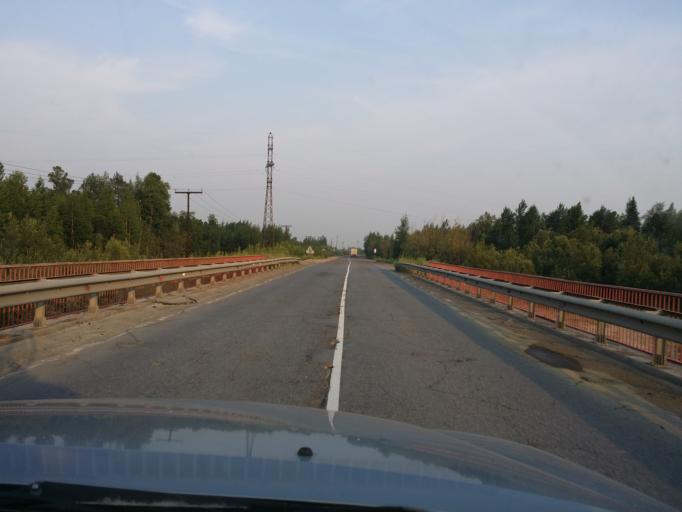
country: RU
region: Khanty-Mansiyskiy Avtonomnyy Okrug
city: Nizhnevartovsk
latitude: 61.1954
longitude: 76.5494
